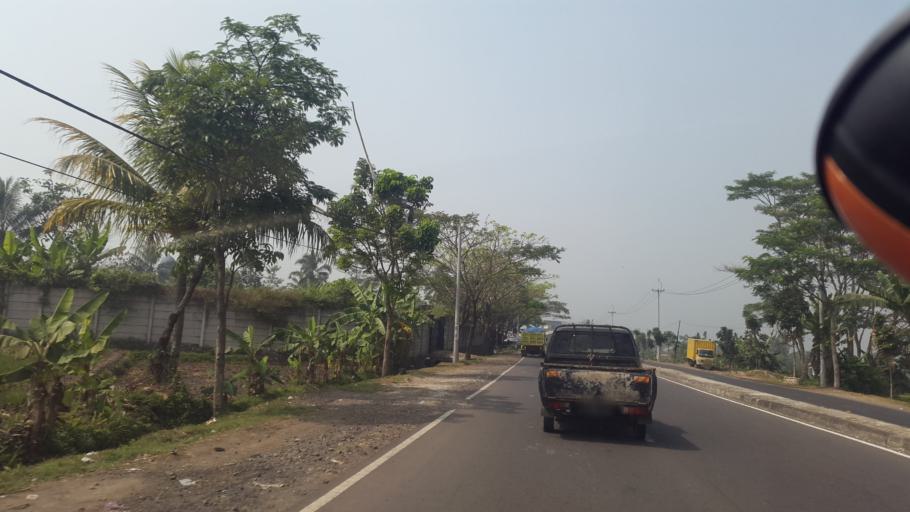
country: ID
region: West Java
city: Sukabumi
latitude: -6.9432
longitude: 106.9126
